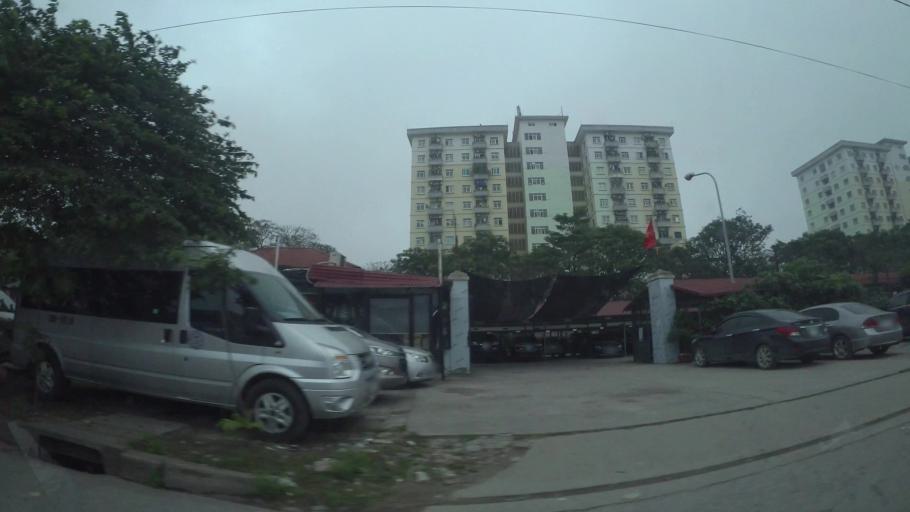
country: VN
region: Ha Noi
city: Thanh Xuan
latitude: 20.9866
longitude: 105.8270
